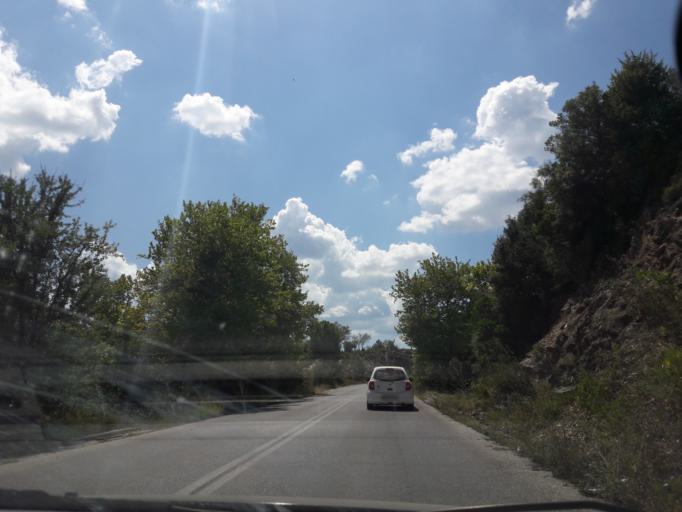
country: GR
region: Central Macedonia
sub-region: Nomos Chalkidikis
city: Polygyros
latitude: 40.3596
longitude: 23.4947
